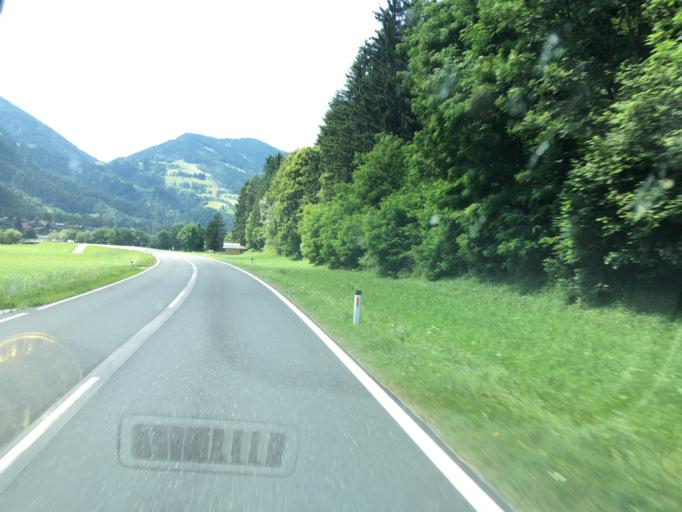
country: AT
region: Carinthia
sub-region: Politischer Bezirk Spittal an der Drau
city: Rangersdorf
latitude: 46.8587
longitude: 12.9419
